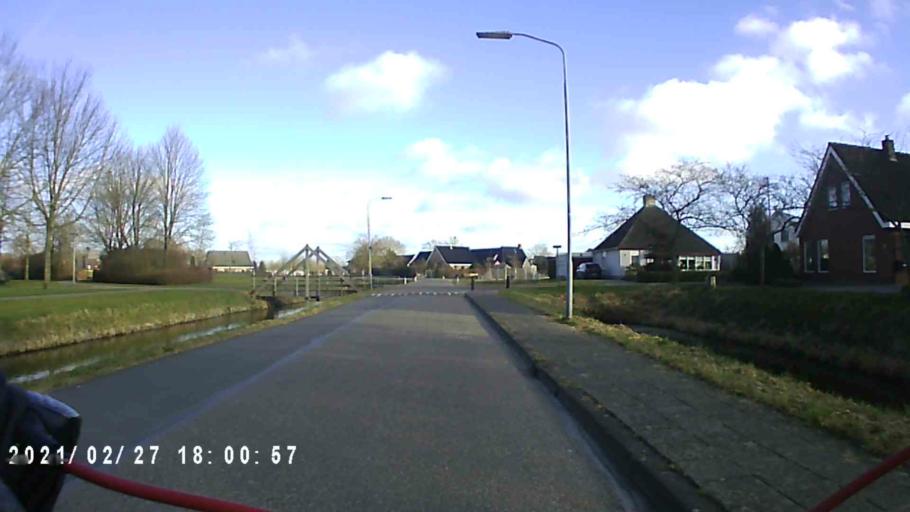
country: NL
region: Groningen
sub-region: Gemeente Bedum
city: Bedum
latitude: 53.3021
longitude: 6.6069
